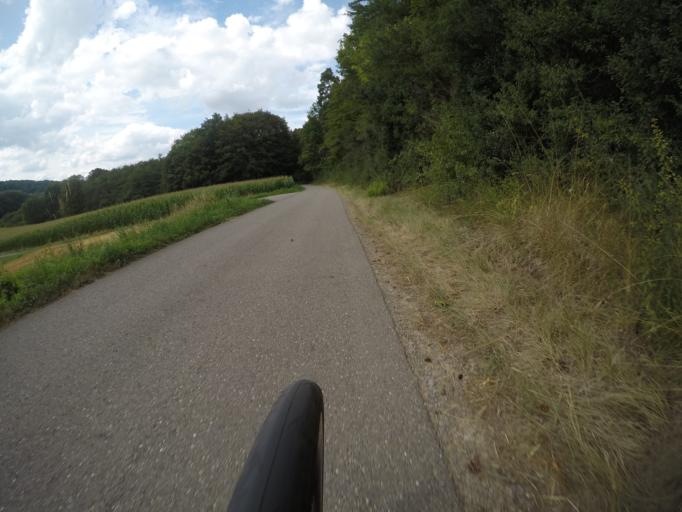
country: DE
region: Baden-Wuerttemberg
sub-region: Regierungsbezirk Stuttgart
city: Weil der Stadt
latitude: 48.7357
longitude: 8.8834
